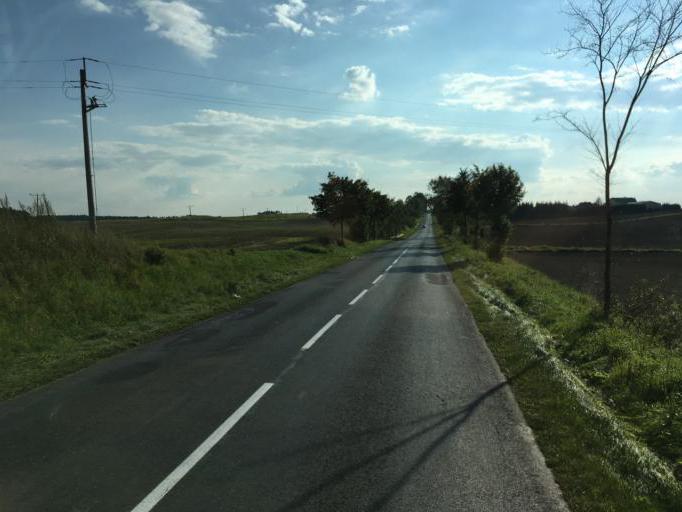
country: PL
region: Kujawsko-Pomorskie
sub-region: Powiat tucholski
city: Gostycyn
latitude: 53.5225
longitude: 17.8486
